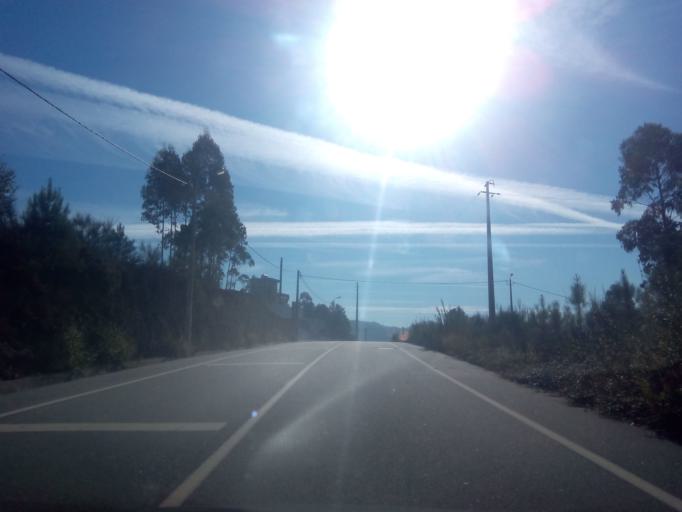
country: PT
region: Porto
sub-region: Paredes
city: Gandra
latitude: 41.2044
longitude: -8.4297
